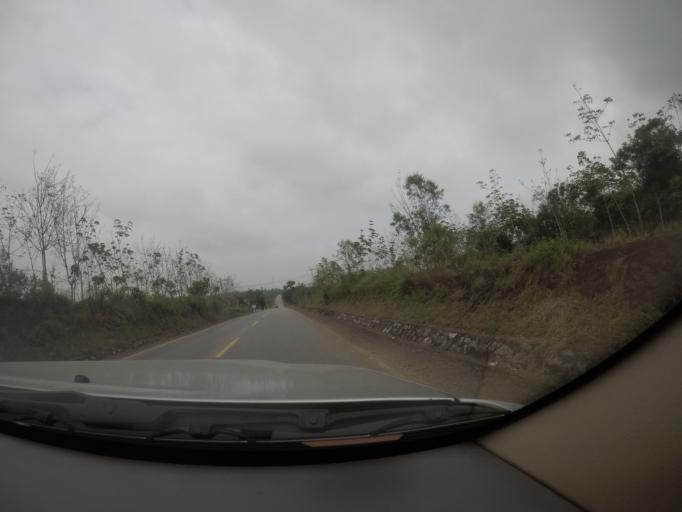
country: VN
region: Quang Binh
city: Hoan Lao
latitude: 17.4910
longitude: 106.5178
